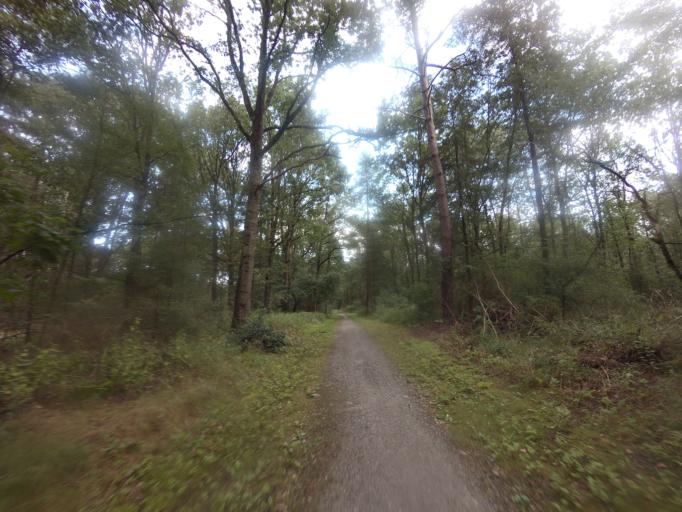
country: NL
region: Overijssel
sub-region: Gemeente Staphorst
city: Staphorst
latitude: 52.6478
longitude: 6.2660
